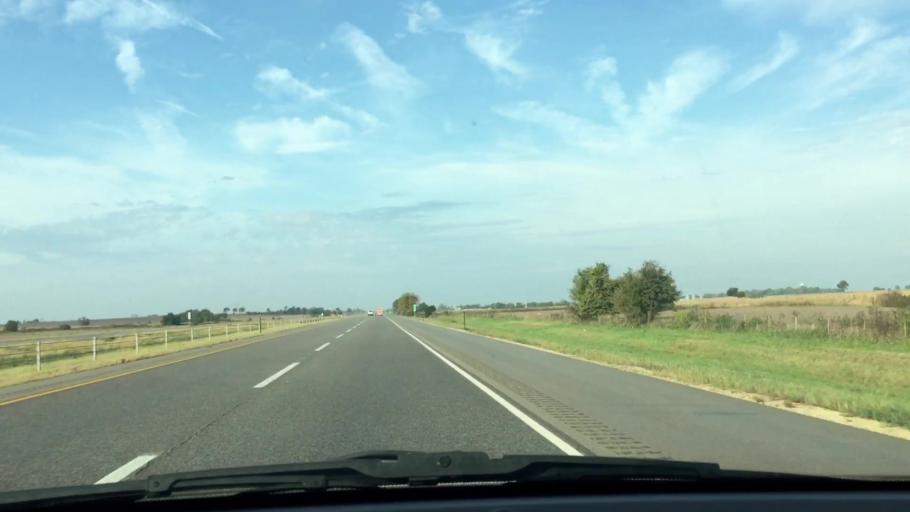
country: US
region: Illinois
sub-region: Ogle County
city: Rochelle
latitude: 41.8675
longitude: -89.1768
